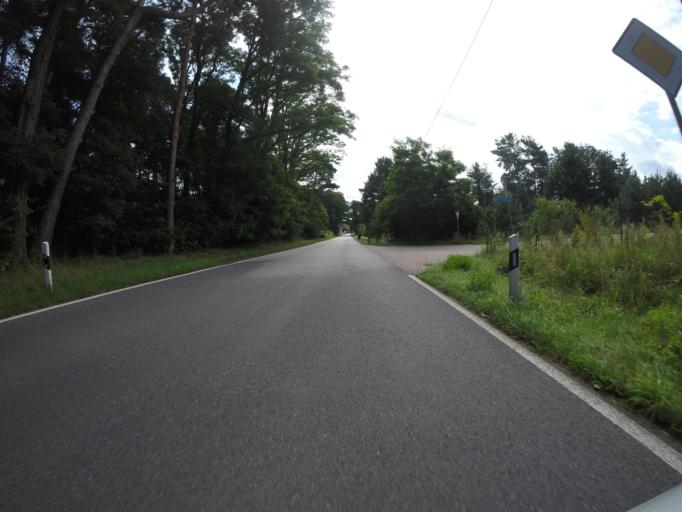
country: DE
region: Brandenburg
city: Grosswoltersdorf
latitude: 53.1040
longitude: 13.0403
